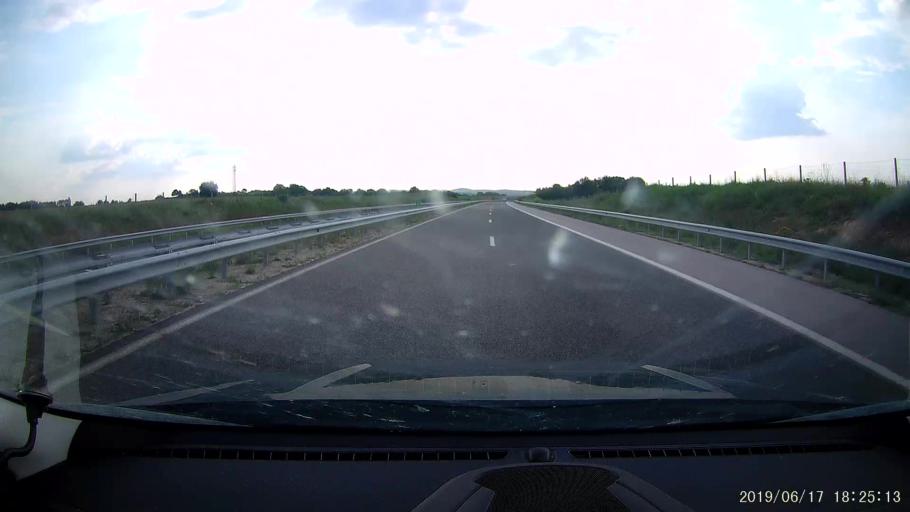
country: BG
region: Khaskovo
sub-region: Obshtina Dimitrovgrad
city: Dimitrovgrad
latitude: 41.9899
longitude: 25.6674
